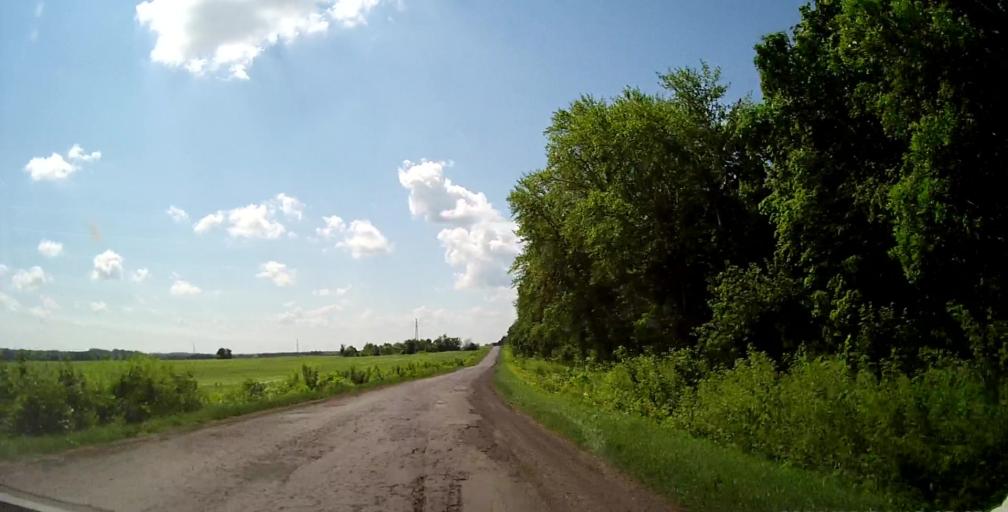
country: RU
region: Lipetsk
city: Chaplygin
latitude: 53.2968
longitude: 39.9551
